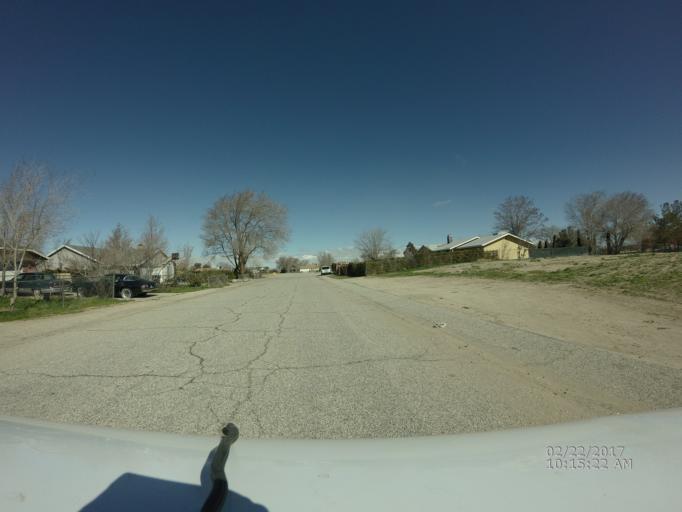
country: US
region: California
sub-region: Los Angeles County
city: Lake Los Angeles
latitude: 34.6286
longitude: -117.8304
